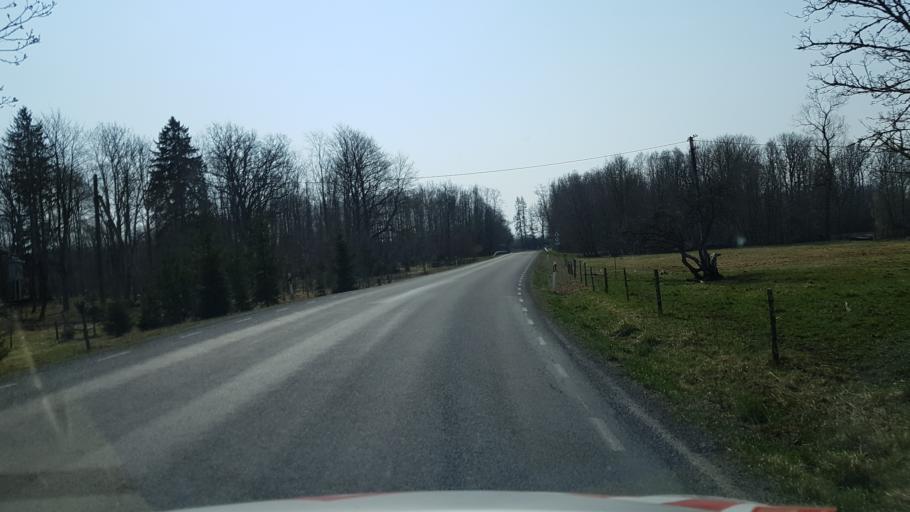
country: EE
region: Raplamaa
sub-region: Kehtna vald
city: Kehtna
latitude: 59.0251
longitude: 24.9268
